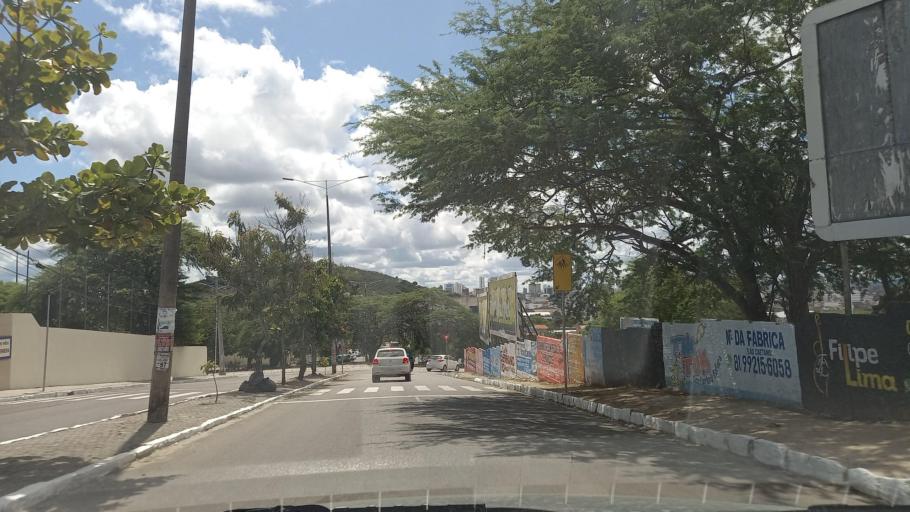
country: BR
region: Pernambuco
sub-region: Caruaru
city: Caruaru
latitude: -8.2972
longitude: -35.9738
